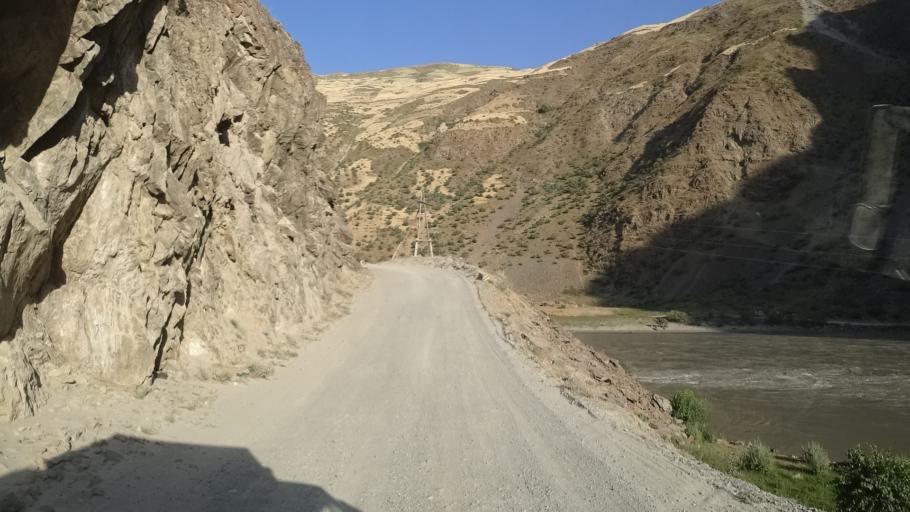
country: AF
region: Badakhshan
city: Maymay
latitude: 38.4763
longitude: 70.9663
